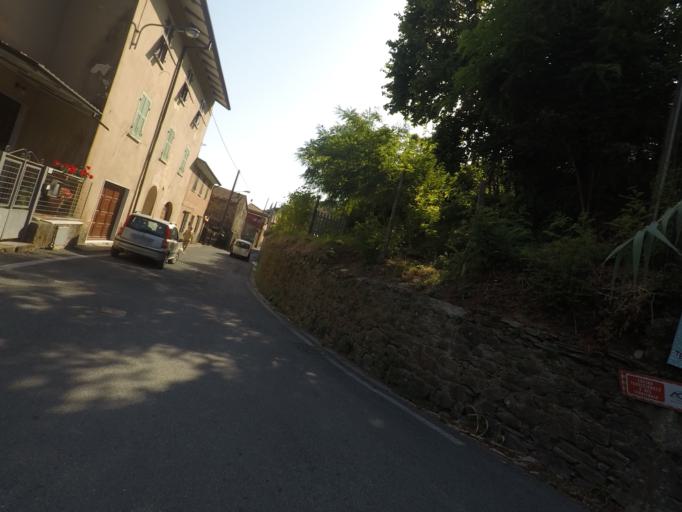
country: IT
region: Liguria
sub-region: Provincia di La Spezia
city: Casano-Dogana-Isola
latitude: 44.0935
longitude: 10.0499
